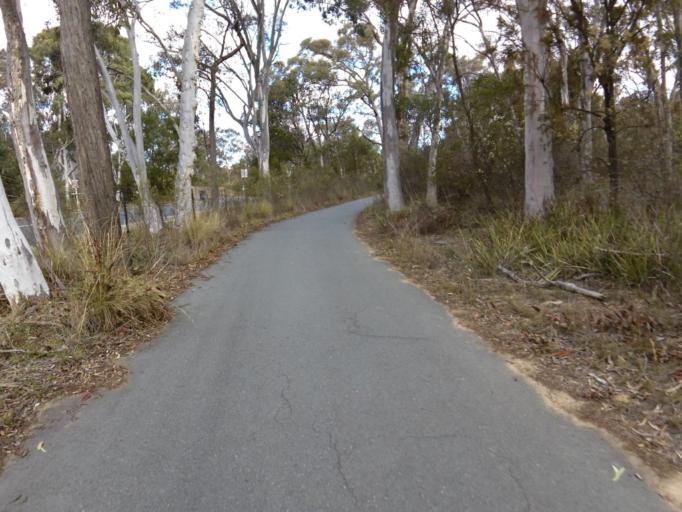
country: AU
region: Australian Capital Territory
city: Macquarie
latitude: -35.2495
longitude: 149.0931
